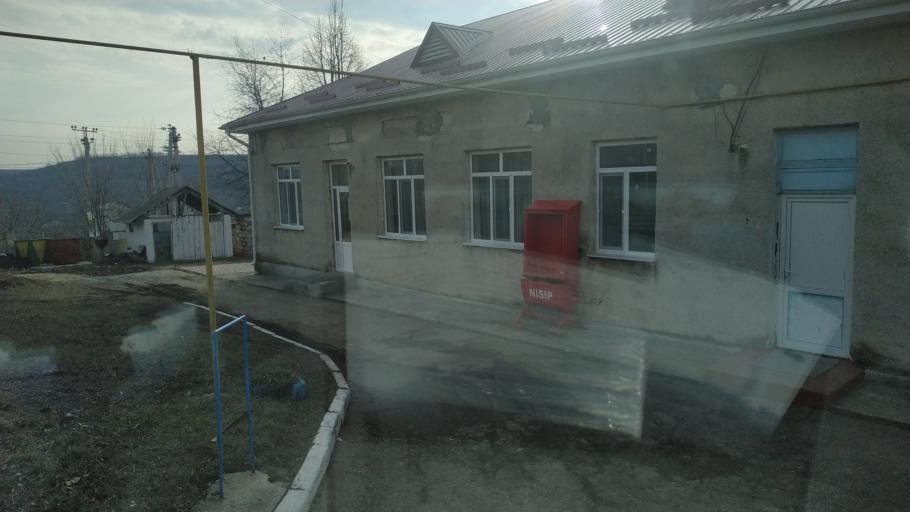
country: MD
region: Chisinau
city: Vadul lui Voda
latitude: 47.0101
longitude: 29.1225
